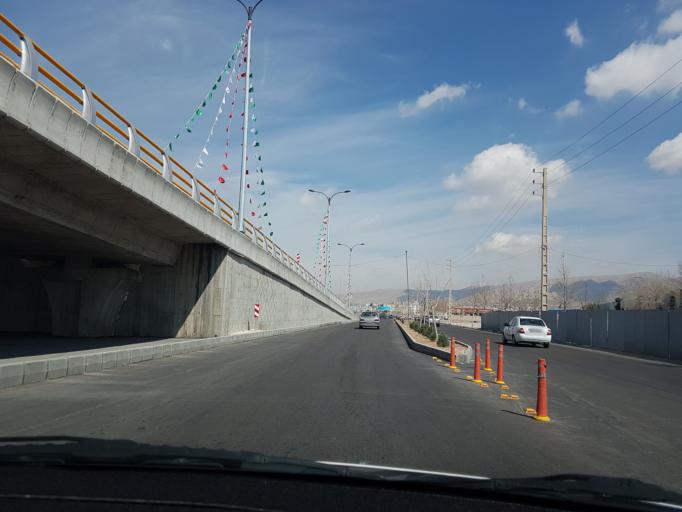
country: IR
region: Fars
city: Shiraz
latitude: 29.6166
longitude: 52.4687
